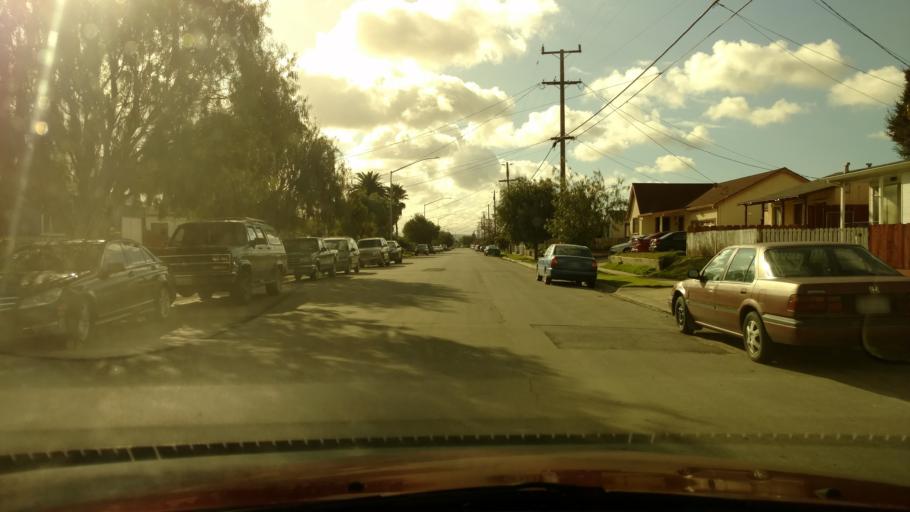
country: US
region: California
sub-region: Monterey County
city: Salinas
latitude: 36.6756
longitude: -121.6117
